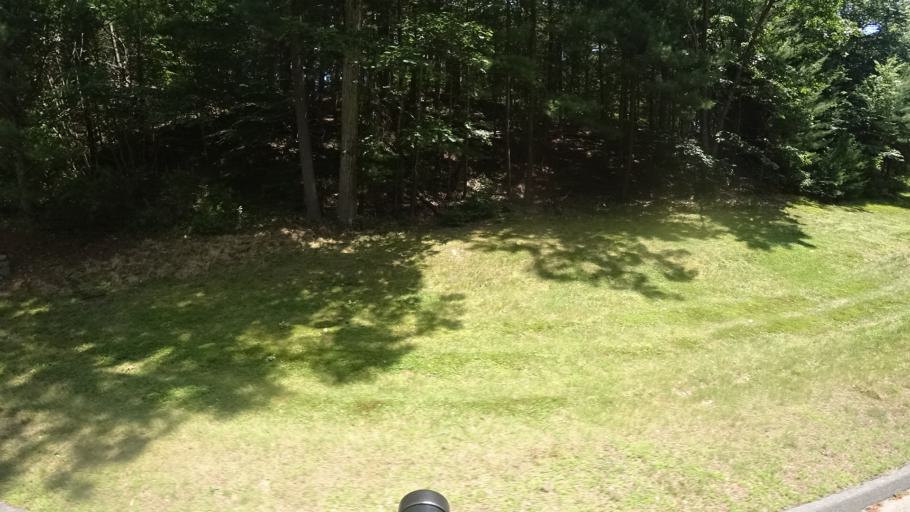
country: US
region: Massachusetts
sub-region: Norfolk County
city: Dedham
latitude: 42.2639
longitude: -71.1962
